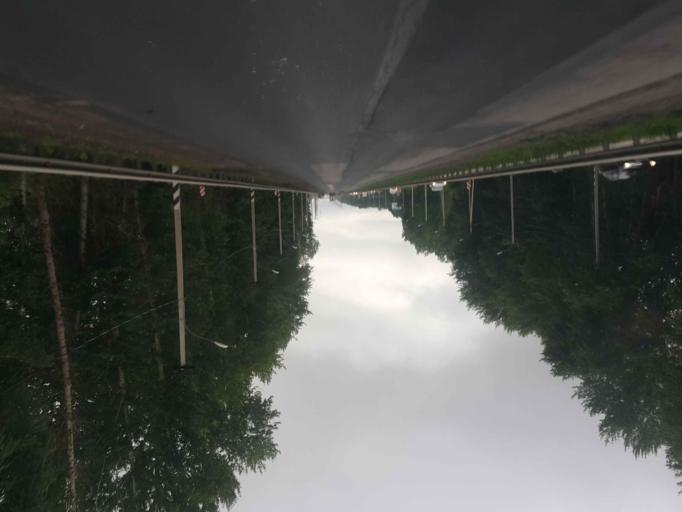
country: RU
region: Tambov
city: Selezni
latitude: 52.7557
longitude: 41.1589
